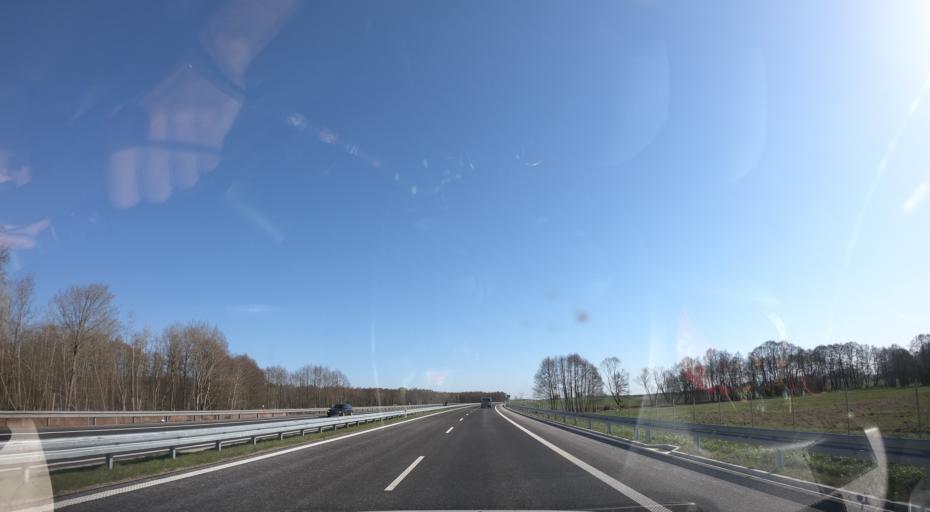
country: PL
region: West Pomeranian Voivodeship
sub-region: Powiat goleniowski
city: Przybiernow
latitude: 53.8068
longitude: 14.7727
